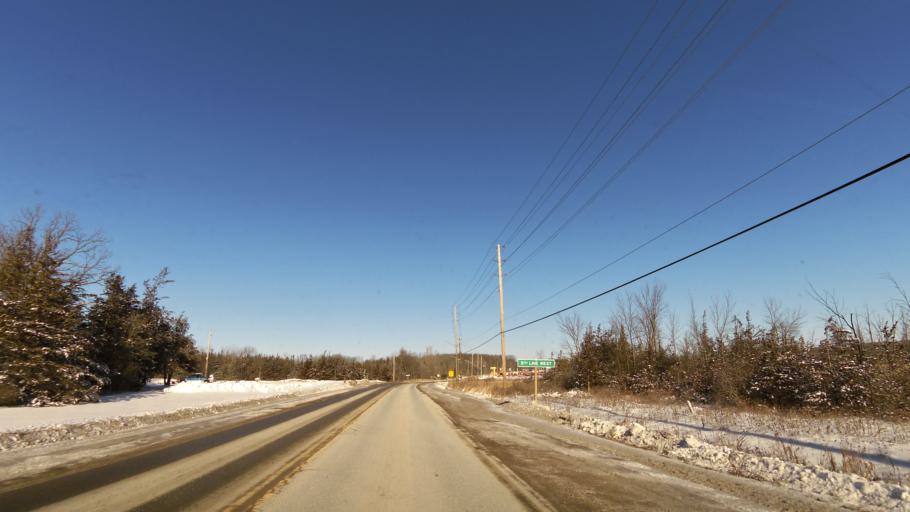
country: CA
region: Ontario
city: Quinte West
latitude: 44.2820
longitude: -77.8087
